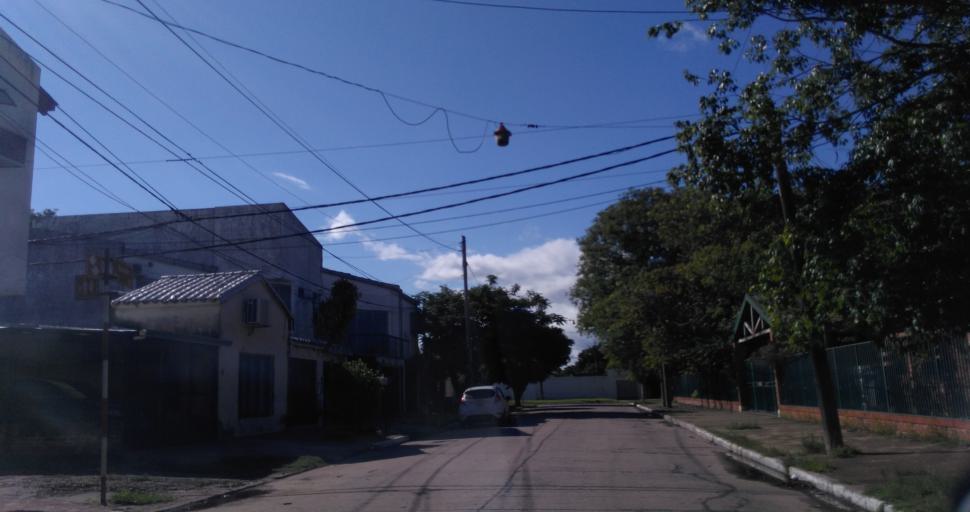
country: AR
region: Chaco
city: Resistencia
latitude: -27.4408
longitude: -58.9765
